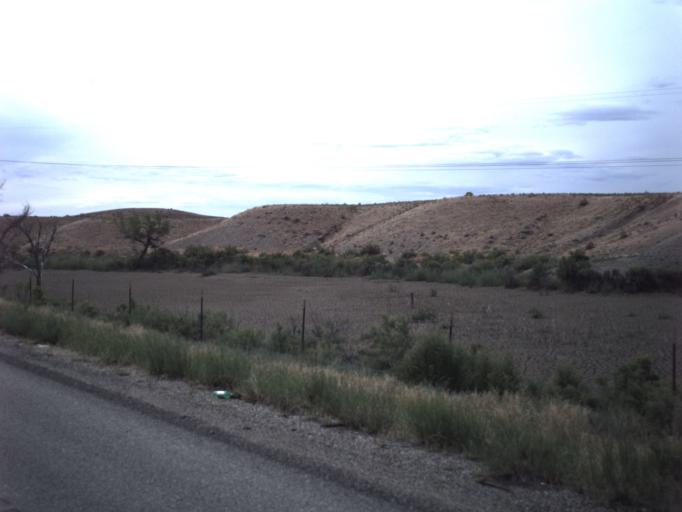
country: US
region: Utah
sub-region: Carbon County
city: East Carbon City
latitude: 39.2609
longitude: -110.3418
